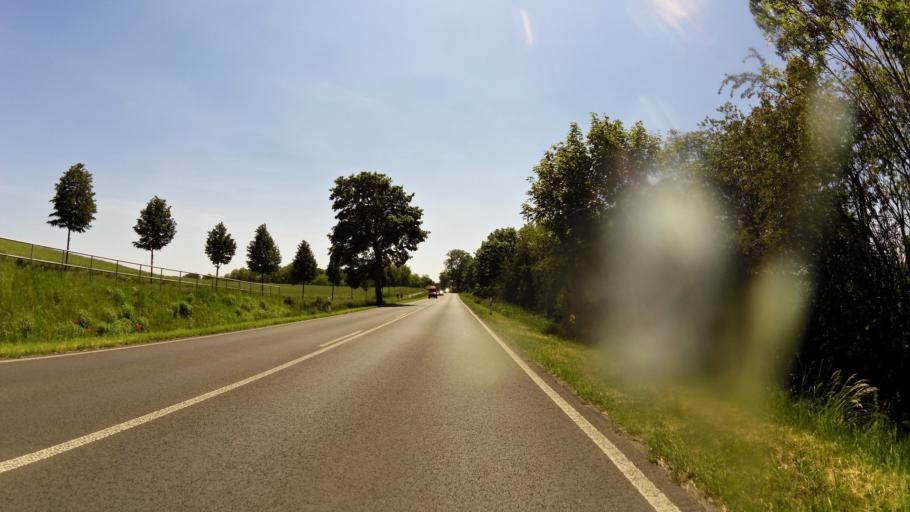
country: DE
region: Brandenburg
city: Lebus
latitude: 52.4134
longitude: 14.5268
